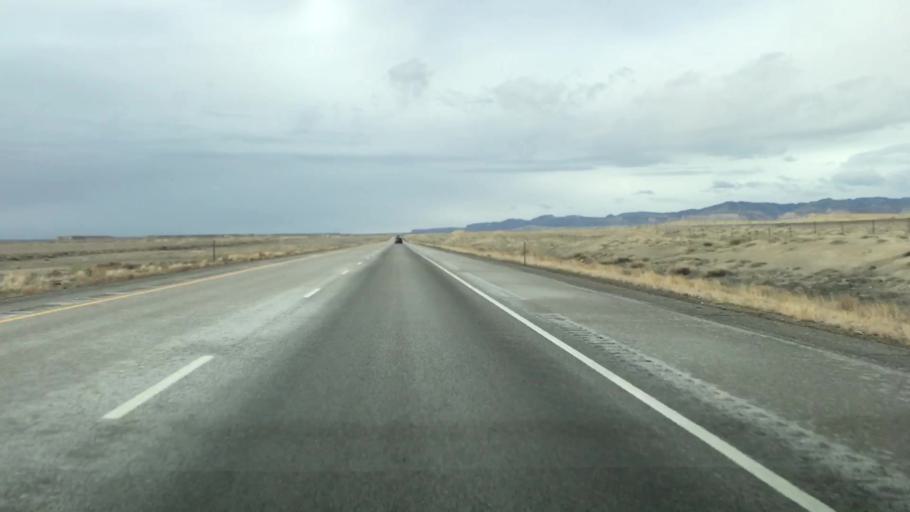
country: US
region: Utah
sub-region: Grand County
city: Moab
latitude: 38.9358
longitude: -109.4565
